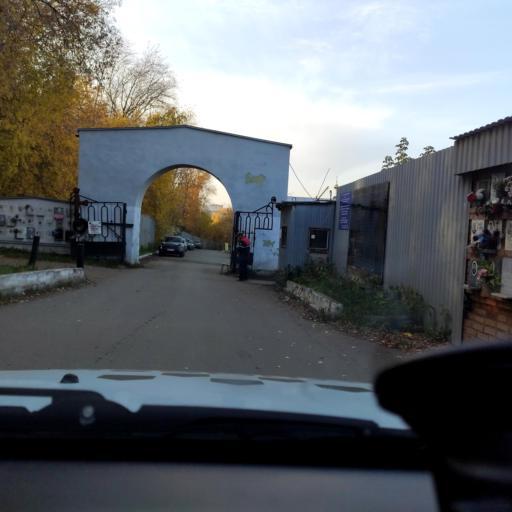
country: RU
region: Perm
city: Perm
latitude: 57.9938
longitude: 56.2804
